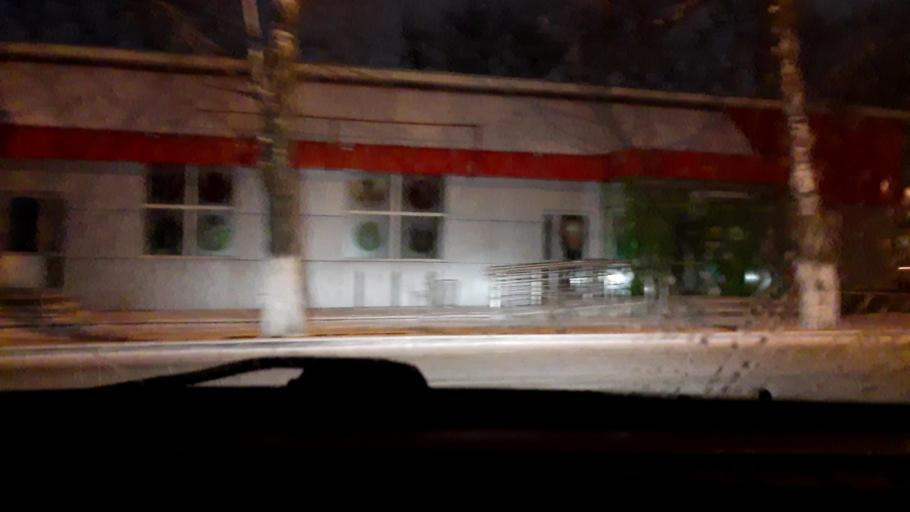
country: RU
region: Nizjnij Novgorod
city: Bor
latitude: 56.3357
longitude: 44.1090
